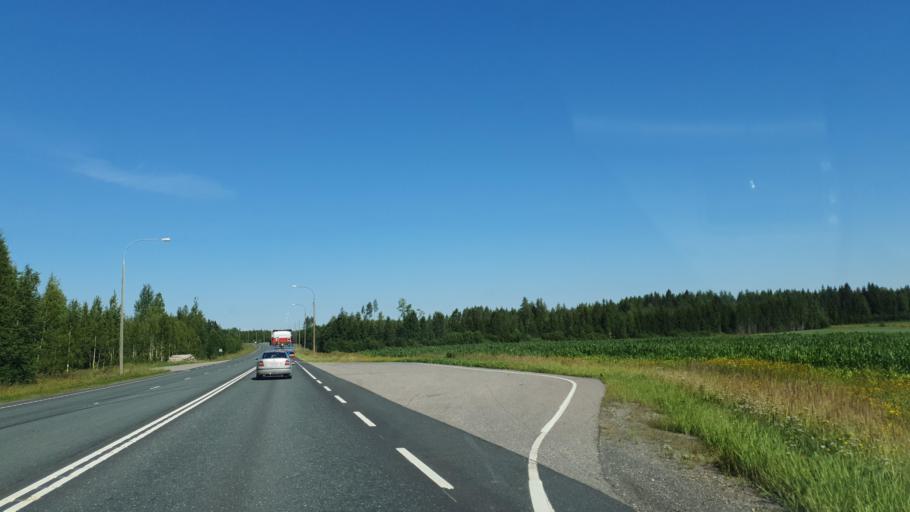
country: FI
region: Northern Savo
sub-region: Ylae-Savo
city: Lapinlahti
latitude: 63.2318
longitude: 27.5040
